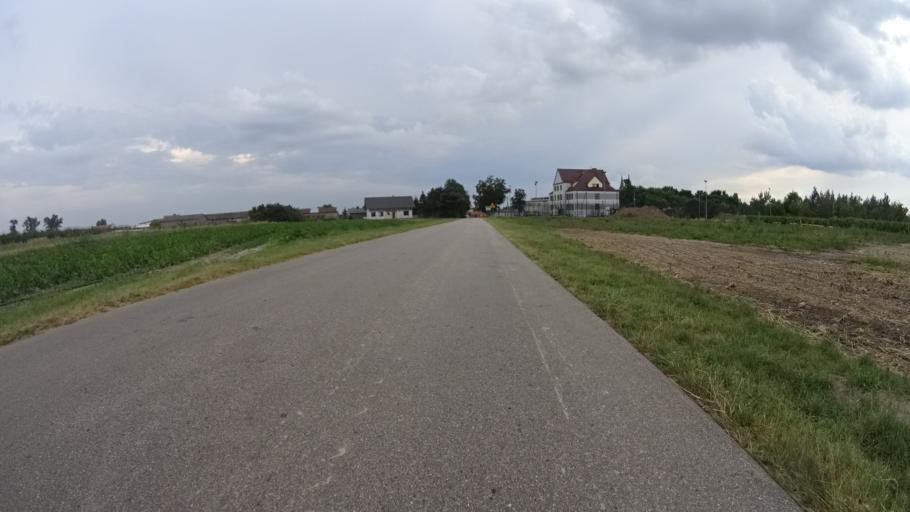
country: PL
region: Masovian Voivodeship
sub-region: Powiat bialobrzeski
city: Wysmierzyce
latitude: 51.6670
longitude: 20.8559
